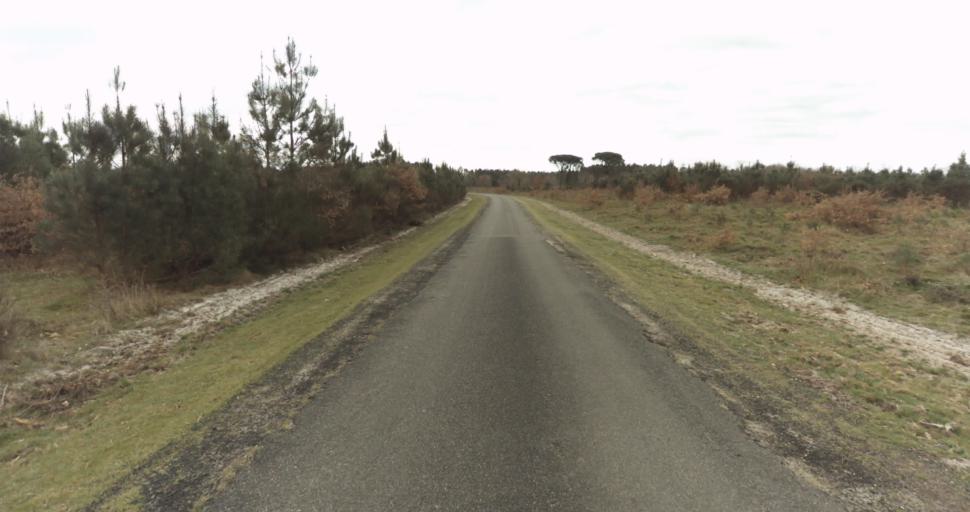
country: FR
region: Aquitaine
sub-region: Departement des Landes
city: Roquefort
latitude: 44.0619
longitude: -0.4309
